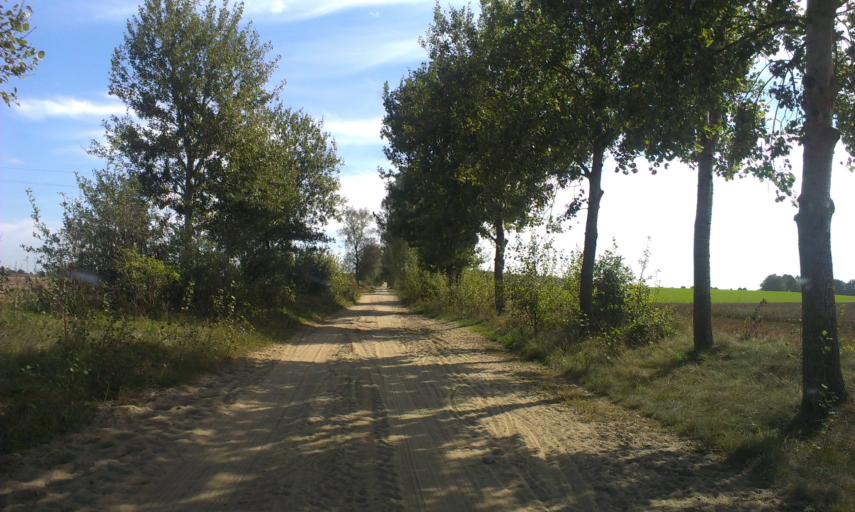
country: PL
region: Greater Poland Voivodeship
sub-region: Powiat pilski
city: Lobzenica
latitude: 53.2946
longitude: 17.1535
